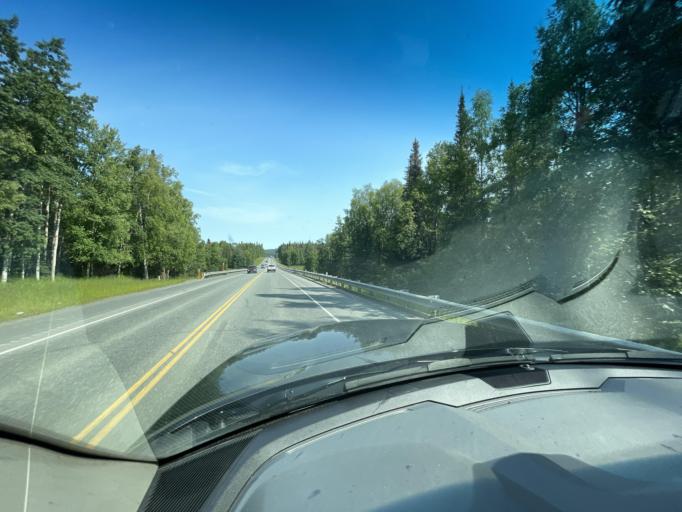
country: US
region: Alaska
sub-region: Kenai Peninsula Borough
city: Soldotna
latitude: 60.4606
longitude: -151.0953
